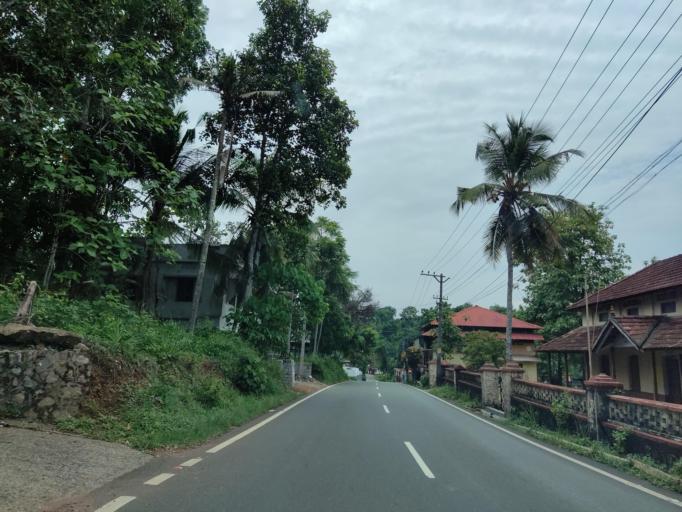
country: IN
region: Kerala
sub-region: Alappuzha
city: Chengannur
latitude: 9.2808
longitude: 76.6149
